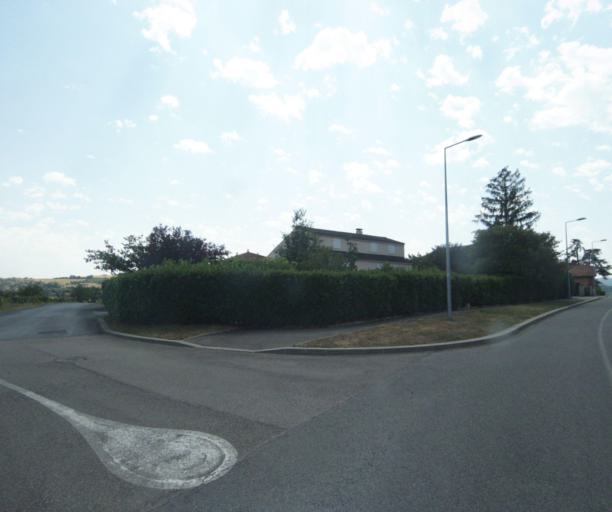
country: FR
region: Rhone-Alpes
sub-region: Departement du Rhone
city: Saint-Germain-Nuelles
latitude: 45.8468
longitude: 4.6217
